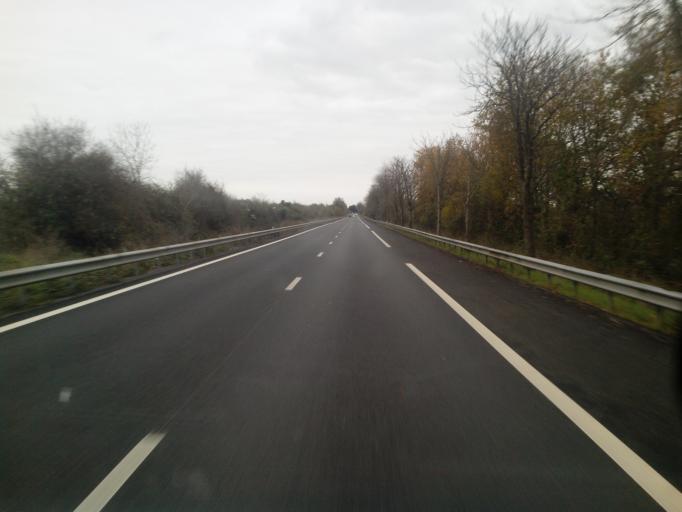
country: FR
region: Pays de la Loire
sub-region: Departement de la Loire-Atlantique
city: La Grigonnais
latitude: 47.4840
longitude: -1.6372
